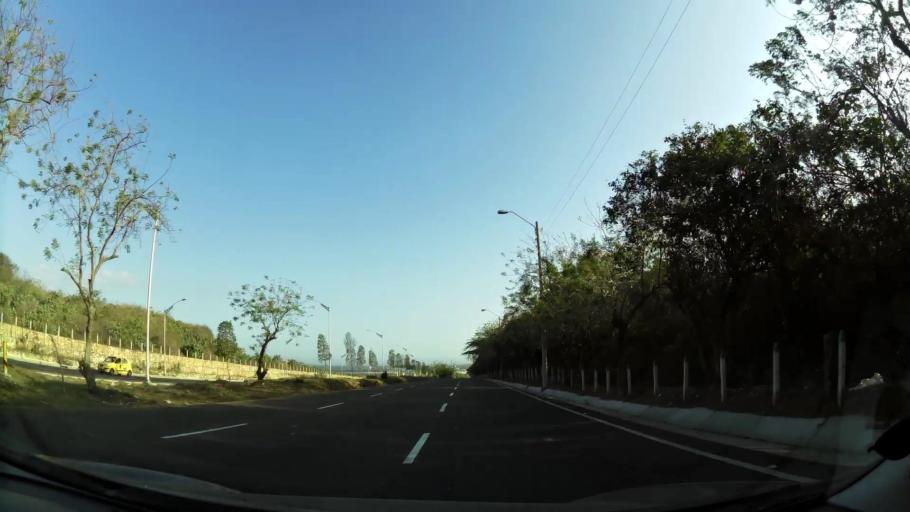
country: CO
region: Atlantico
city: Barranquilla
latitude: 11.0255
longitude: -74.8345
